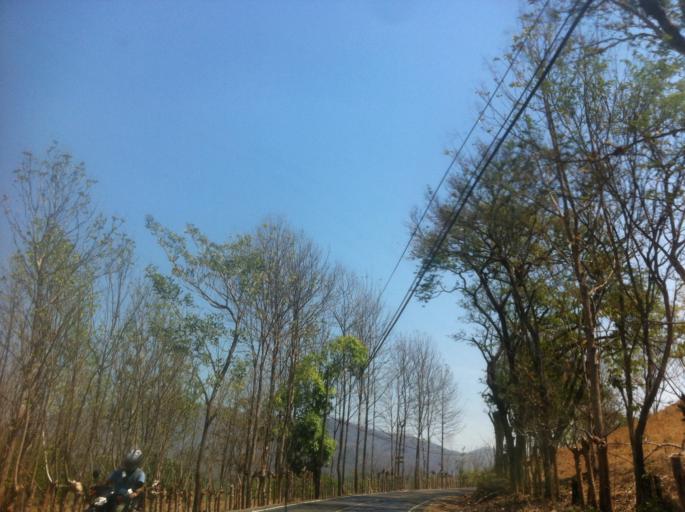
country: CR
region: Guanacaste
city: Hojancha
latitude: 10.0747
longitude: -85.4708
